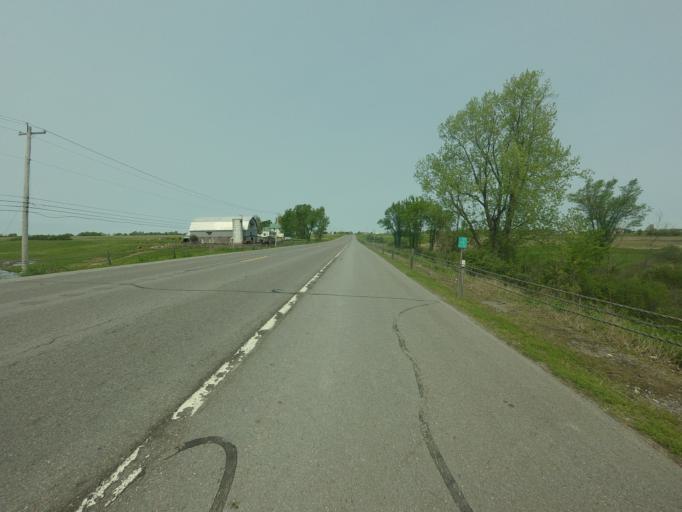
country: US
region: New York
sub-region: Jefferson County
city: Dexter
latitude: 44.0525
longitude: -76.1029
